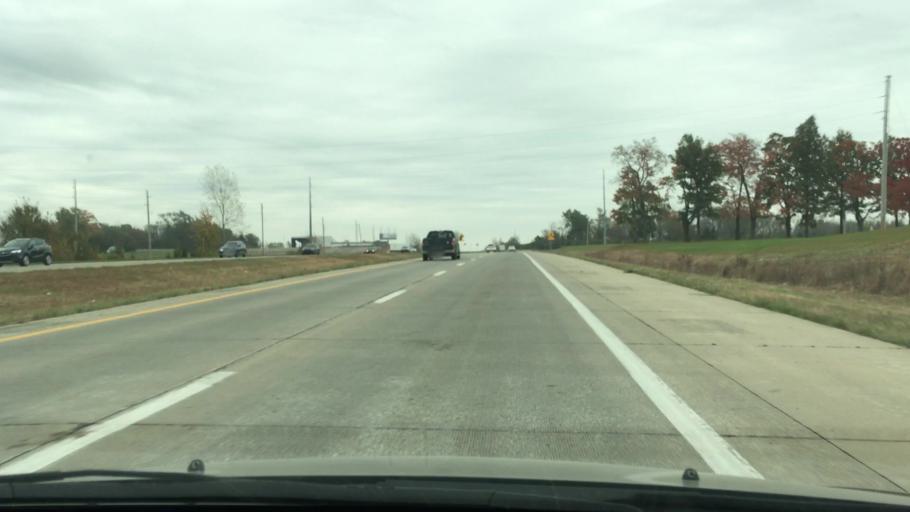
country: US
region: Missouri
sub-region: Jackson County
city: Grandview
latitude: 38.8599
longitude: -94.5693
